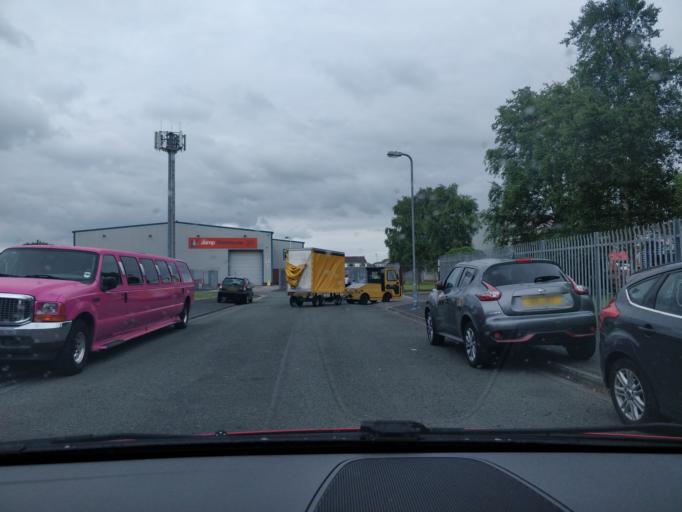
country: GB
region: England
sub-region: Lancashire
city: Banks
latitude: 53.6728
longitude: -2.9622
